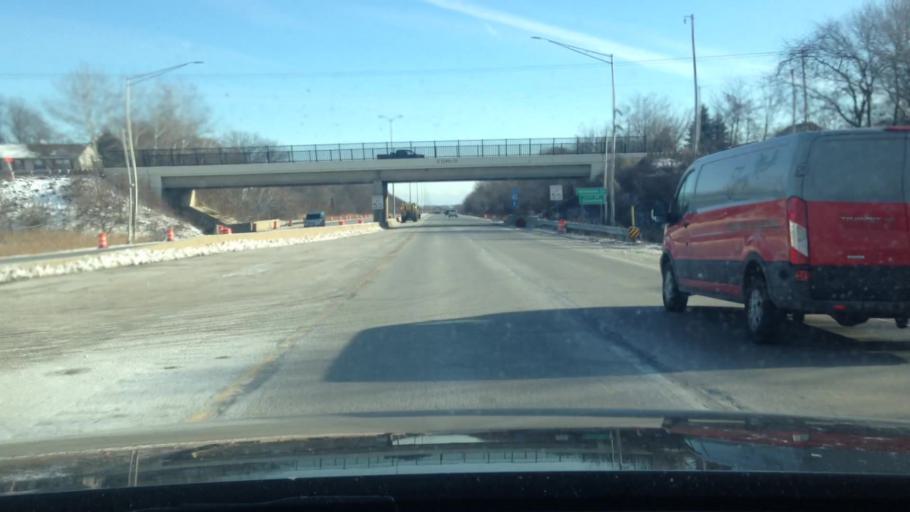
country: US
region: Wisconsin
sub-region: Milwaukee County
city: Hales Corners
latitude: 42.9575
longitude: -88.0703
